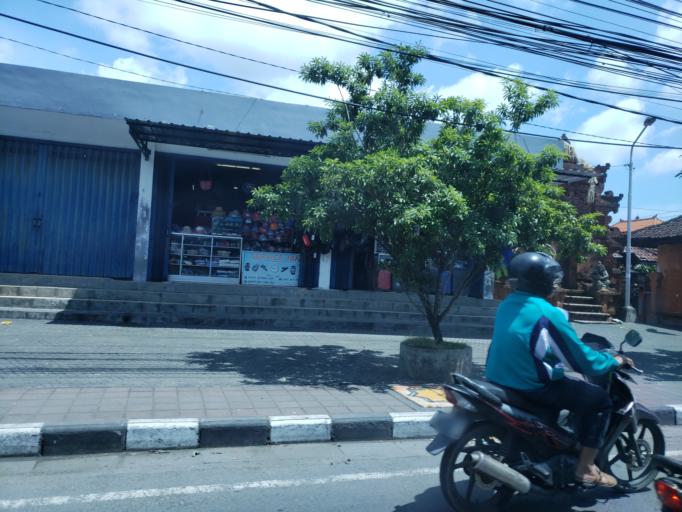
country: ID
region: Bali
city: Kelanabian
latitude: -8.7712
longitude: 115.1731
